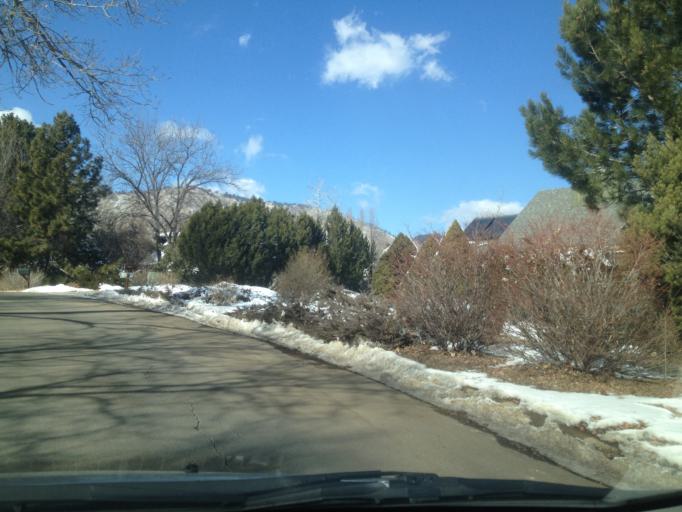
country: US
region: Colorado
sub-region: Boulder County
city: Boulder
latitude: 40.0467
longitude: -105.2861
